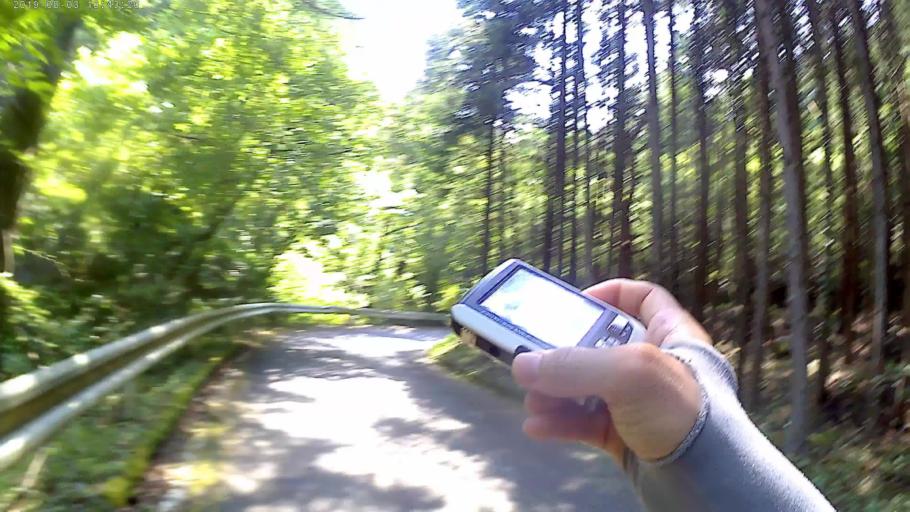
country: JP
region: Yamanashi
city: Enzan
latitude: 35.6231
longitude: 138.7704
